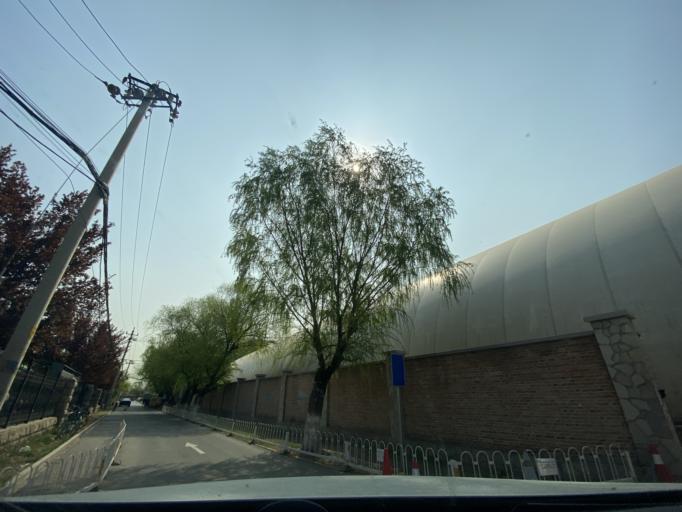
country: CN
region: Beijing
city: Sijiqing
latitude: 39.9425
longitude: 116.2511
